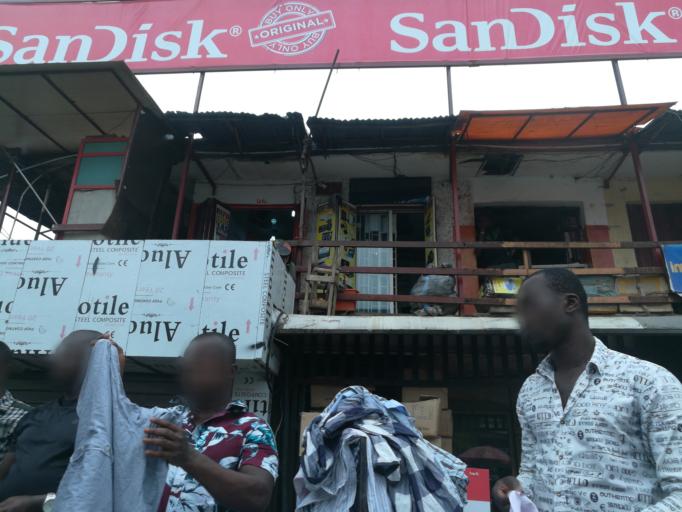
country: NG
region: Lagos
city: Ikeja
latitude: 6.5953
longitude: 3.3406
